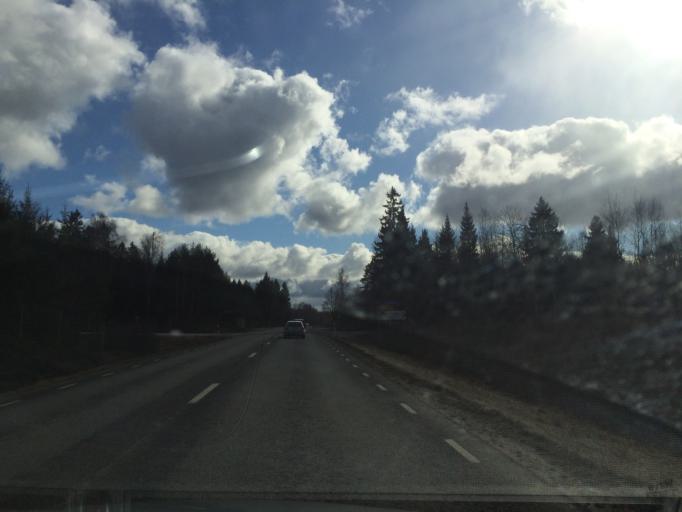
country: SE
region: Vaestra Goetaland
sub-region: Skara Kommun
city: Skara
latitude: 58.3419
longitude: 13.4351
